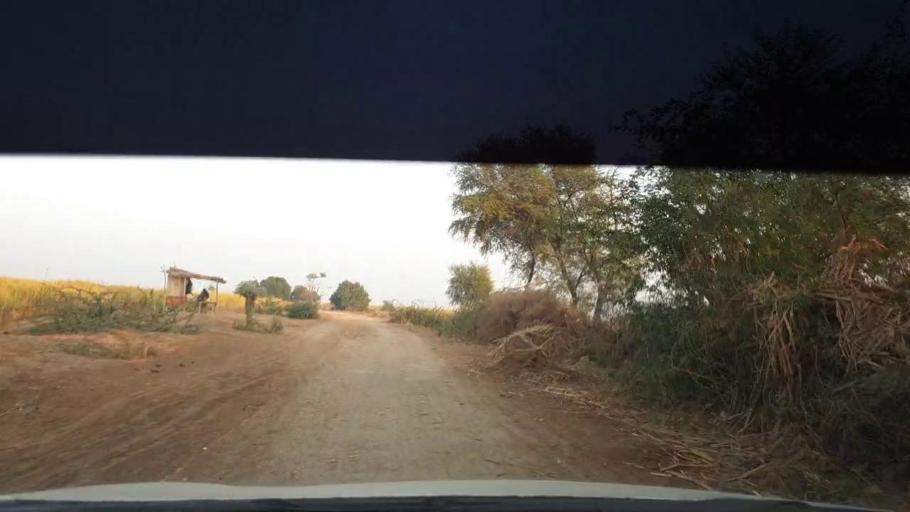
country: PK
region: Sindh
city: Berani
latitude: 25.7531
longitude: 69.0052
